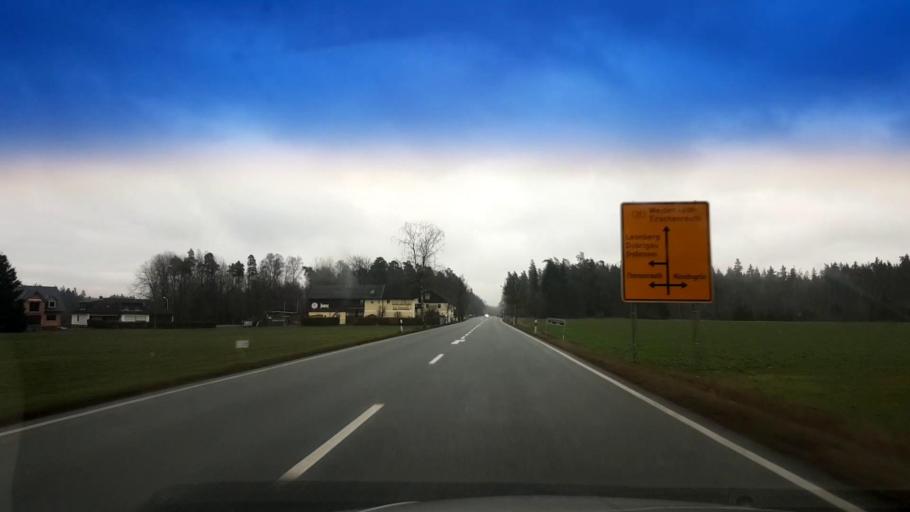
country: DE
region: Bavaria
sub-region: Upper Palatinate
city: Leonberg
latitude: 49.9292
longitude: 12.2768
